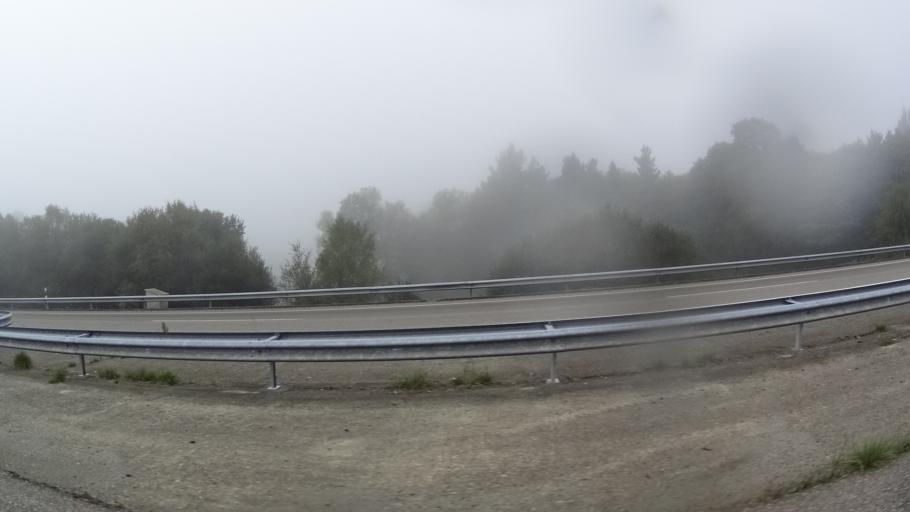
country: ES
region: Galicia
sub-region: Provincia de Lugo
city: Guitiriz
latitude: 43.1909
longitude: -7.8662
